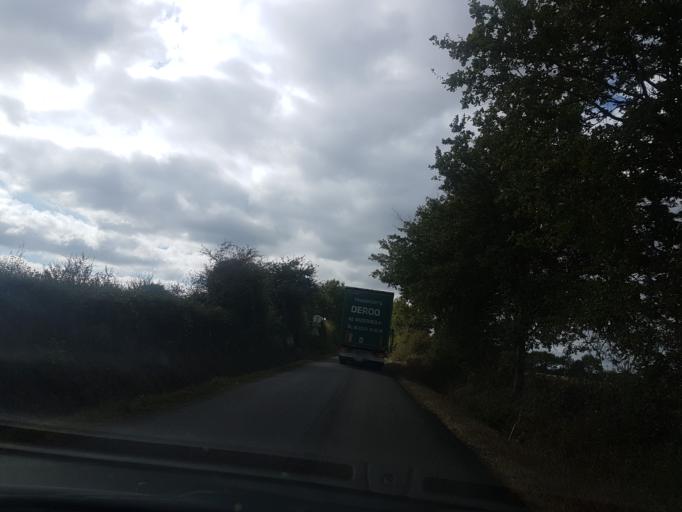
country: FR
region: Pays de la Loire
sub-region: Departement de la Loire-Atlantique
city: Ligne
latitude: 47.3972
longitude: -1.4052
